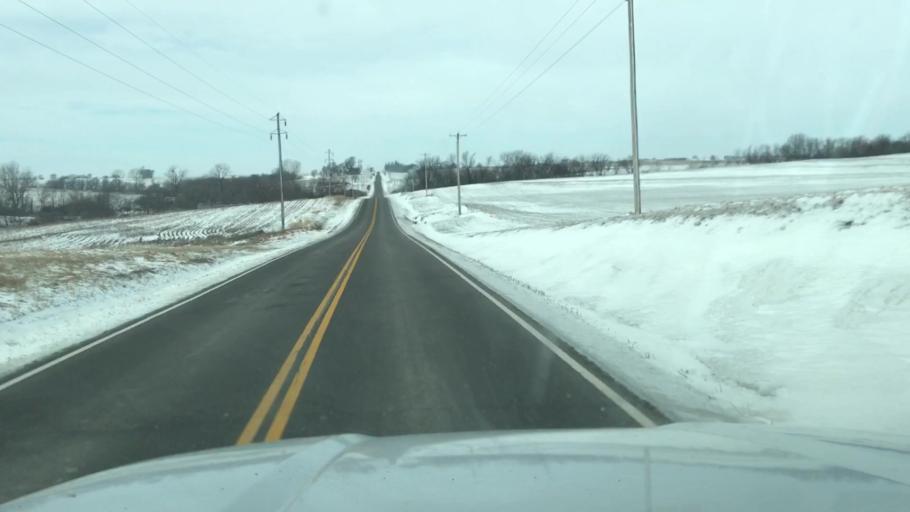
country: US
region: Missouri
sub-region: Holt County
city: Mound City
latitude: 40.1301
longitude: -95.1081
